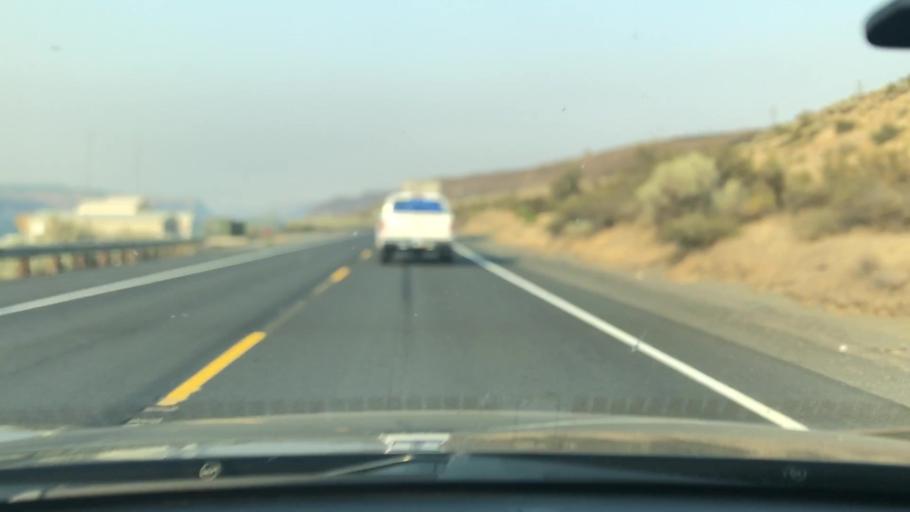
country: US
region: Oregon
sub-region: Umatilla County
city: Stanfield
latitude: 45.9291
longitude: -119.0996
